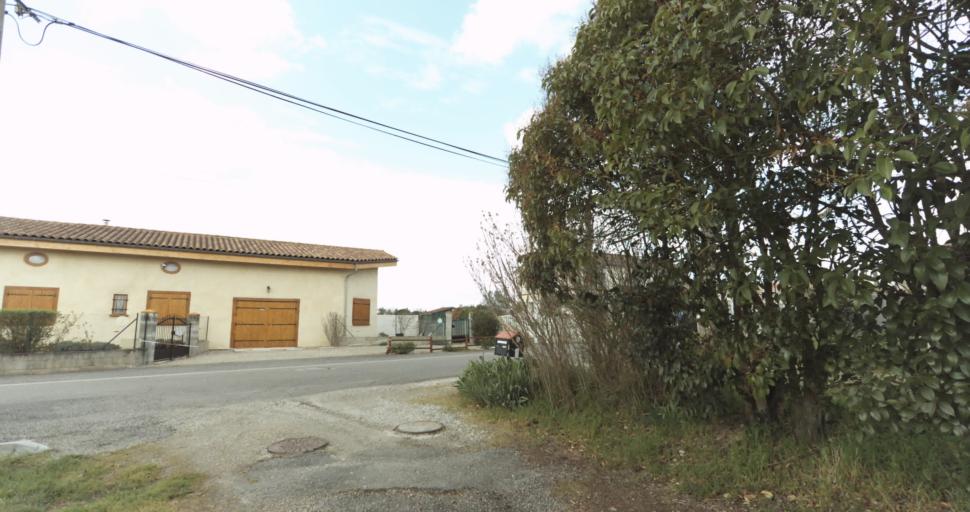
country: FR
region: Midi-Pyrenees
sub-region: Departement de la Haute-Garonne
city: Auterive
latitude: 43.3561
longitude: 1.4792
